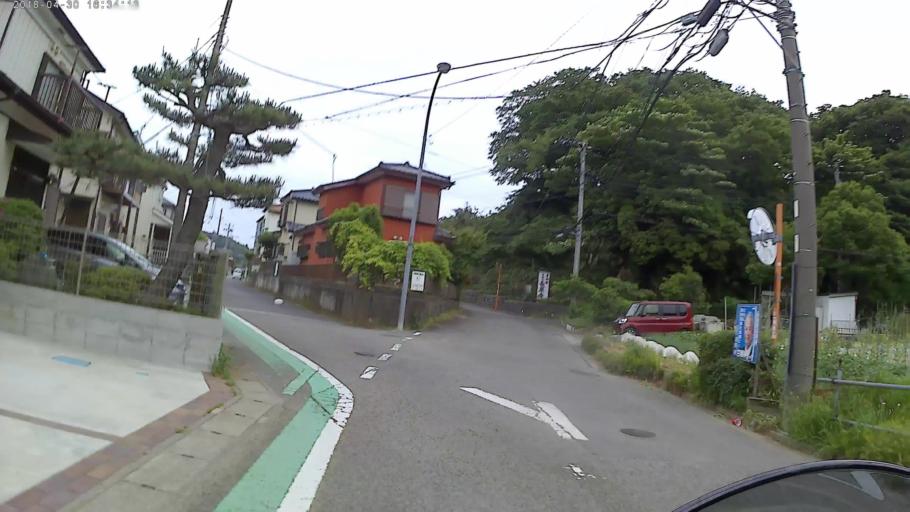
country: JP
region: Kanagawa
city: Zama
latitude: 35.4471
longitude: 139.4073
